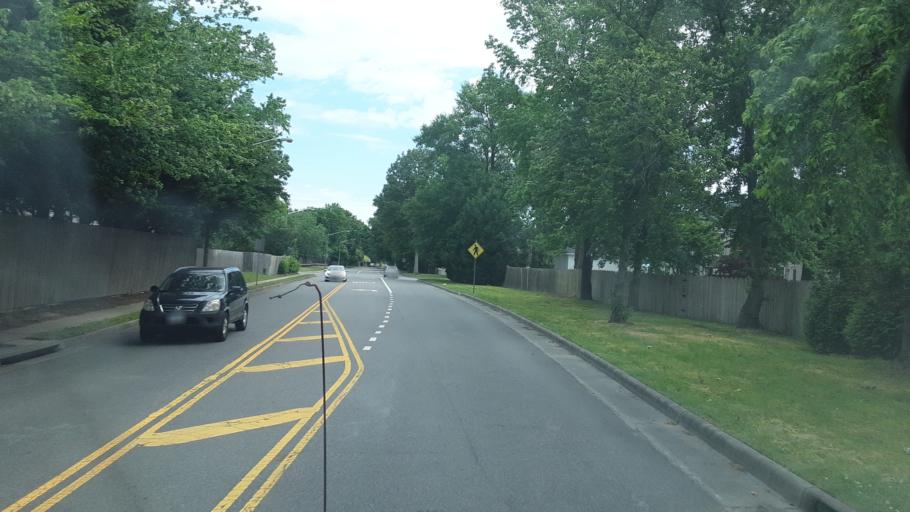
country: US
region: Virginia
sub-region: City of Virginia Beach
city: Virginia Beach
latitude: 36.7651
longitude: -76.0022
